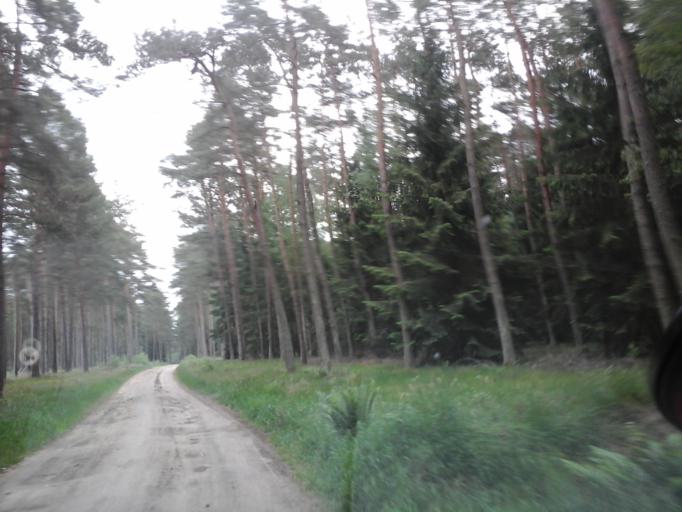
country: PL
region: West Pomeranian Voivodeship
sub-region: Powiat choszczenski
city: Drawno
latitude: 53.1409
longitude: 15.7130
